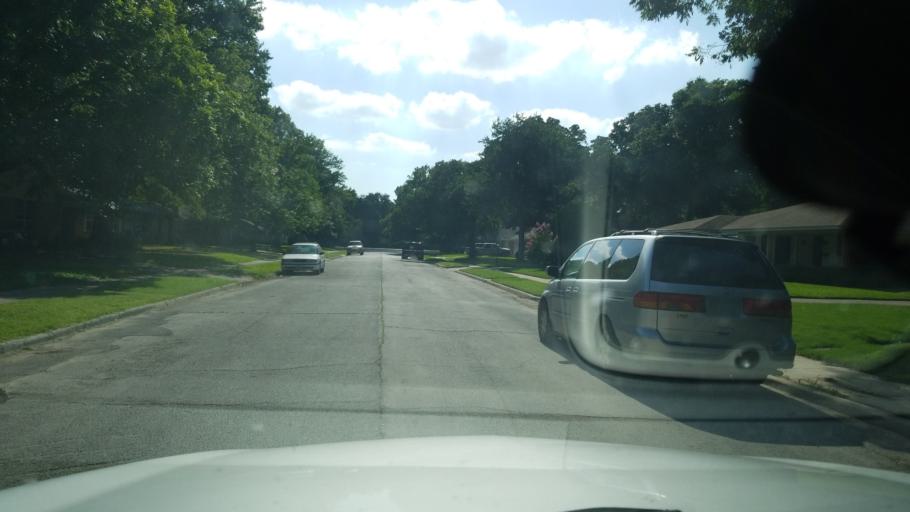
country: US
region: Texas
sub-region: Dallas County
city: Irving
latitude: 32.8210
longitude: -96.9722
